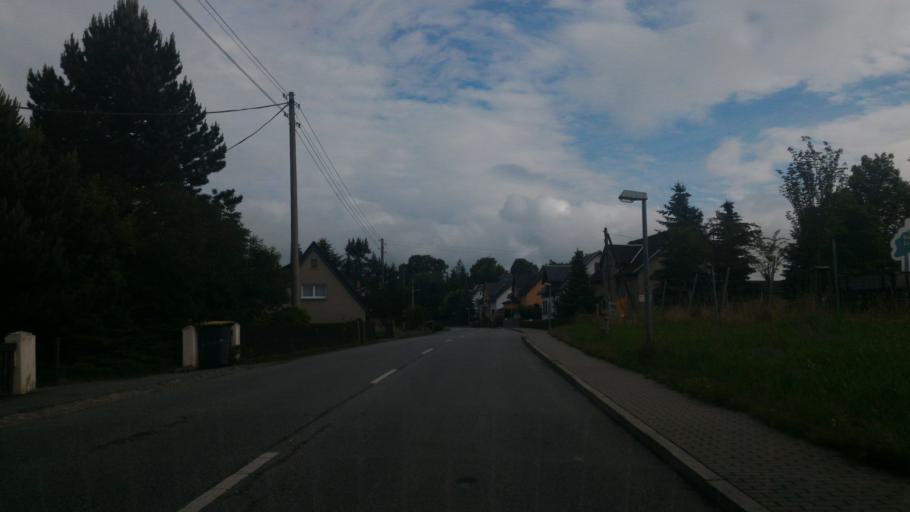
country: DE
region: Saxony
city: Leutersdorf
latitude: 50.9662
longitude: 14.6489
